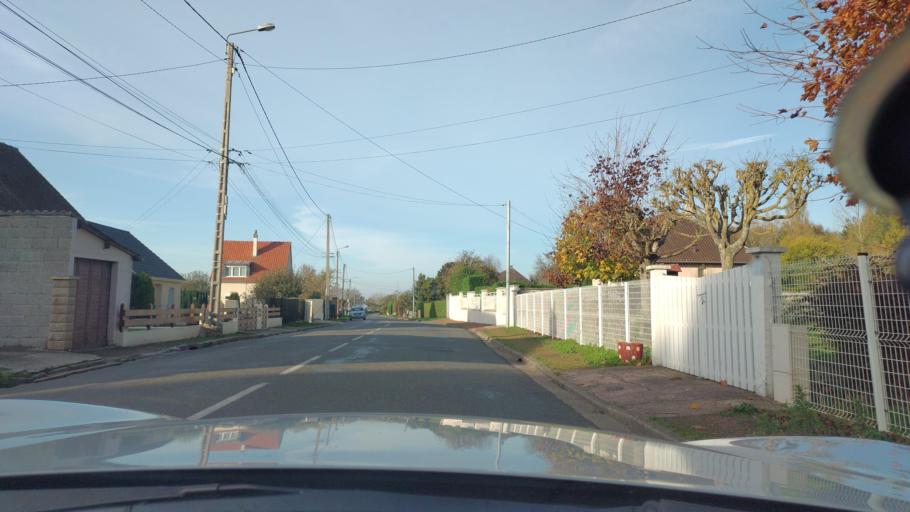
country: FR
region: Picardie
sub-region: Departement de la Somme
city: Friville-Escarbotin
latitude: 50.1072
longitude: 1.5272
